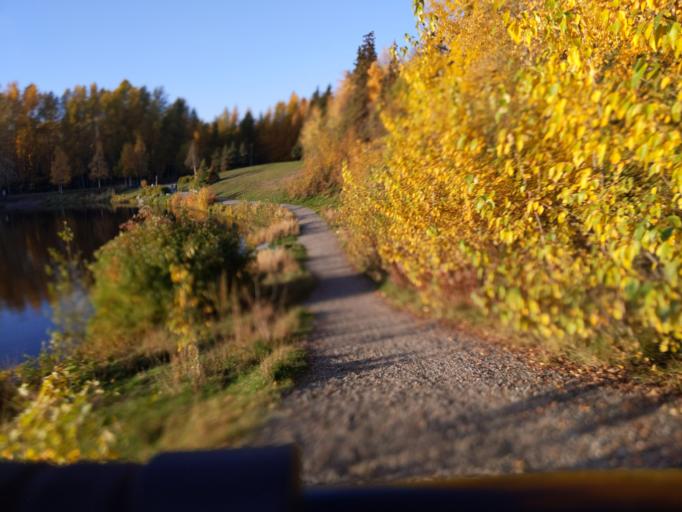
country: US
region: Alaska
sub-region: Anchorage Municipality
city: Anchorage
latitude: 61.1504
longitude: -149.8795
